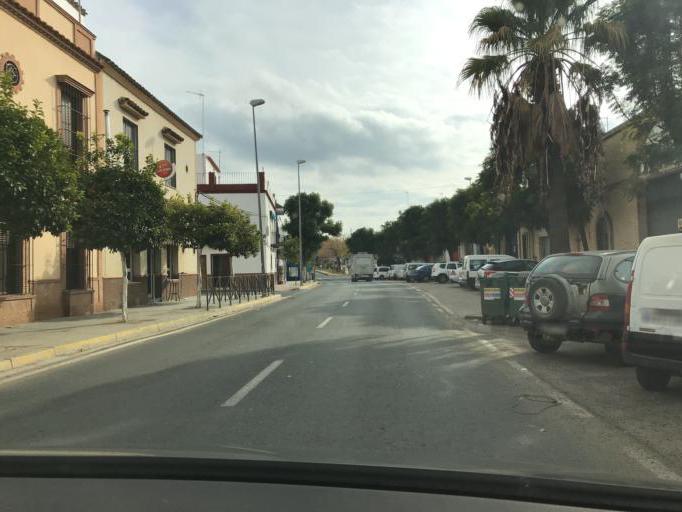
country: ES
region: Andalusia
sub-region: Provincia de Sevilla
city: La Campana
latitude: 37.5700
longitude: -5.4301
